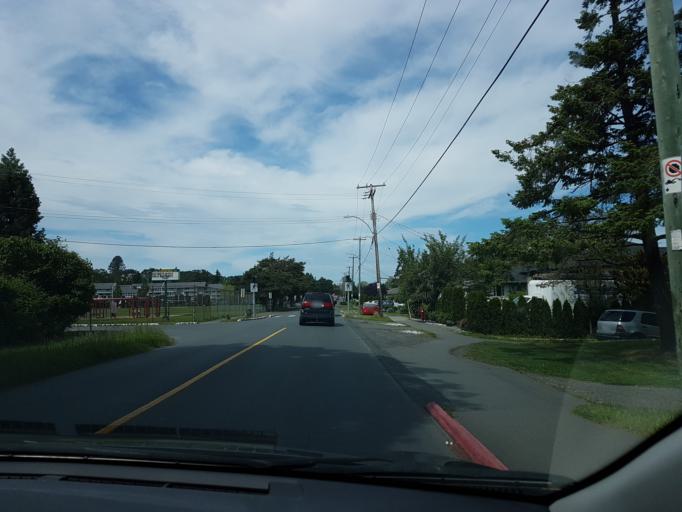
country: CA
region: British Columbia
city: Oak Bay
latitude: 48.4651
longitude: -123.3362
